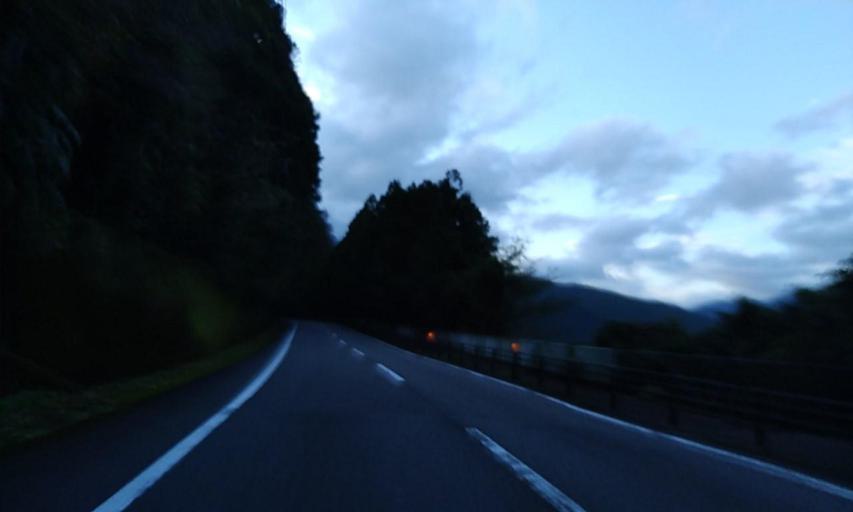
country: JP
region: Wakayama
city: Shingu
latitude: 33.7305
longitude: 135.9476
